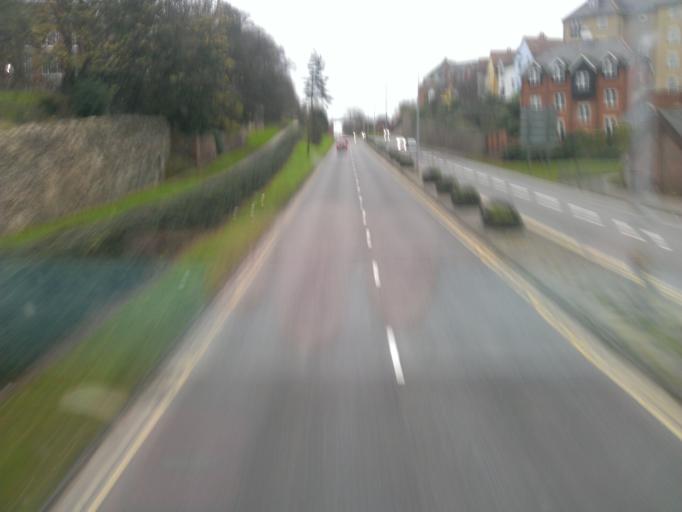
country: GB
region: England
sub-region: Essex
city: Colchester
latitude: 51.8920
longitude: 0.8939
